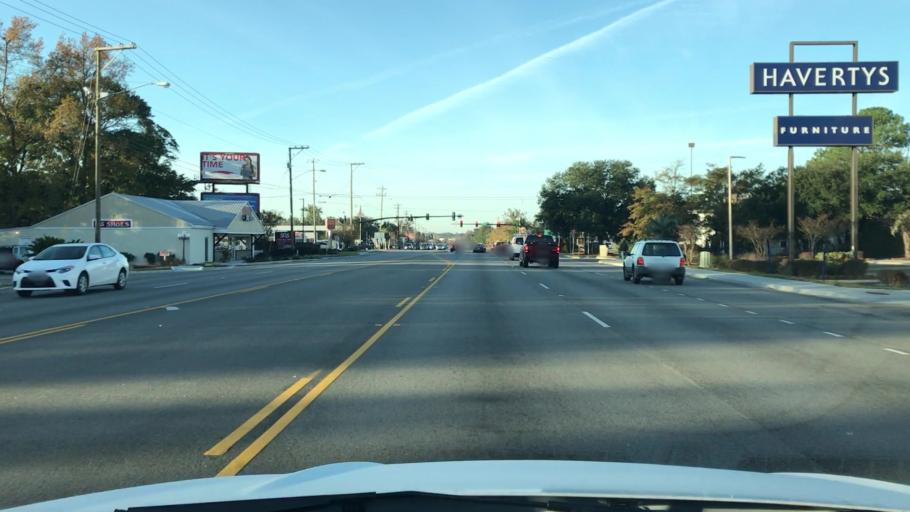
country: US
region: South Carolina
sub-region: Charleston County
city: North Charleston
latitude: 32.8029
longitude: -80.0156
